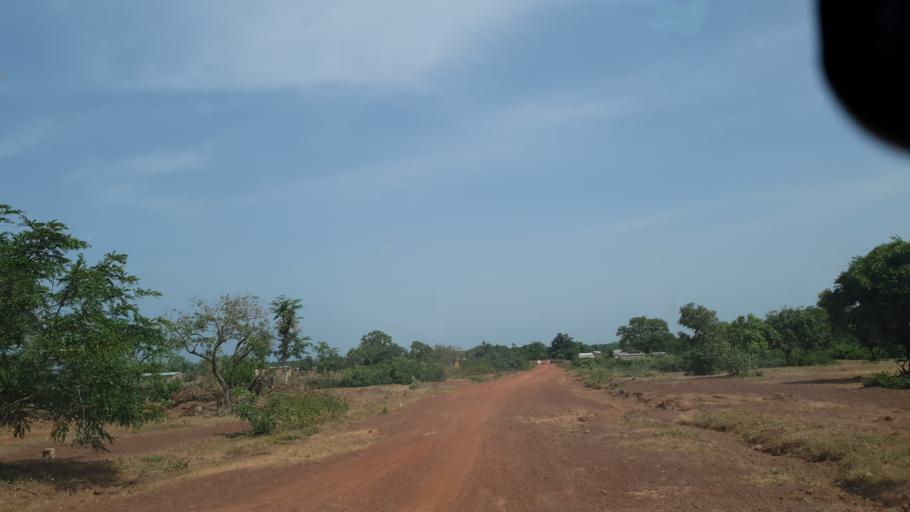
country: ML
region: Koulikoro
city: Dioila
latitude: 12.4750
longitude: -6.1851
